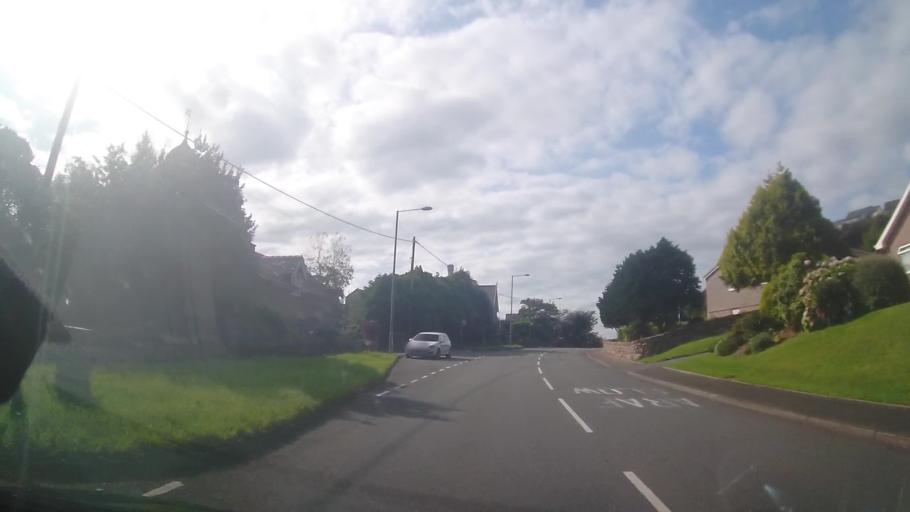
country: GB
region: Wales
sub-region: Gwynedd
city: Barmouth
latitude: 52.7309
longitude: -4.0620
